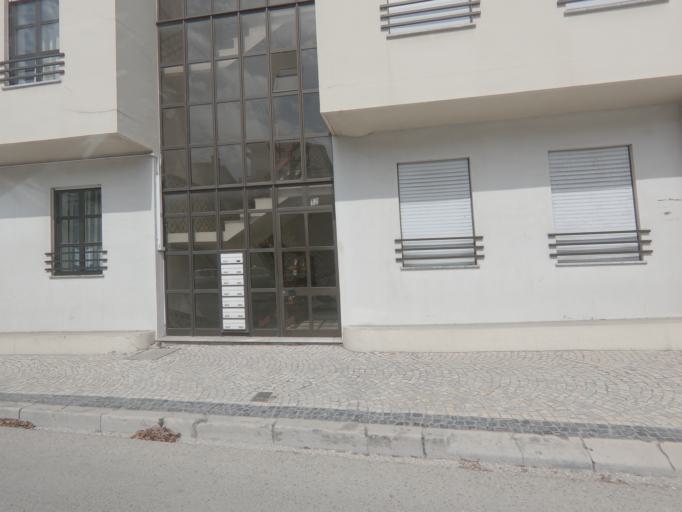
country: PT
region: Leiria
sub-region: Leiria
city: Leiria
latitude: 39.7424
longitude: -8.8114
